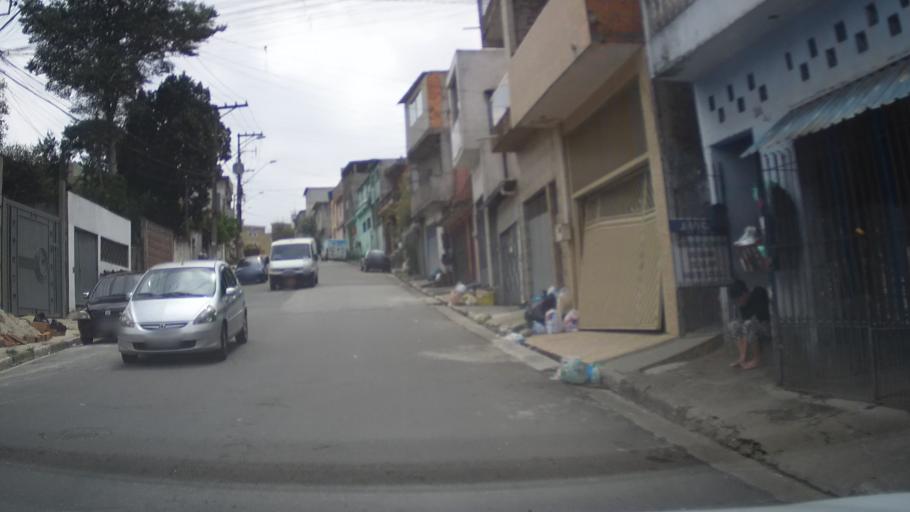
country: BR
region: Sao Paulo
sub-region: Itaquaquecetuba
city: Itaquaquecetuba
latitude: -23.4357
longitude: -46.4123
